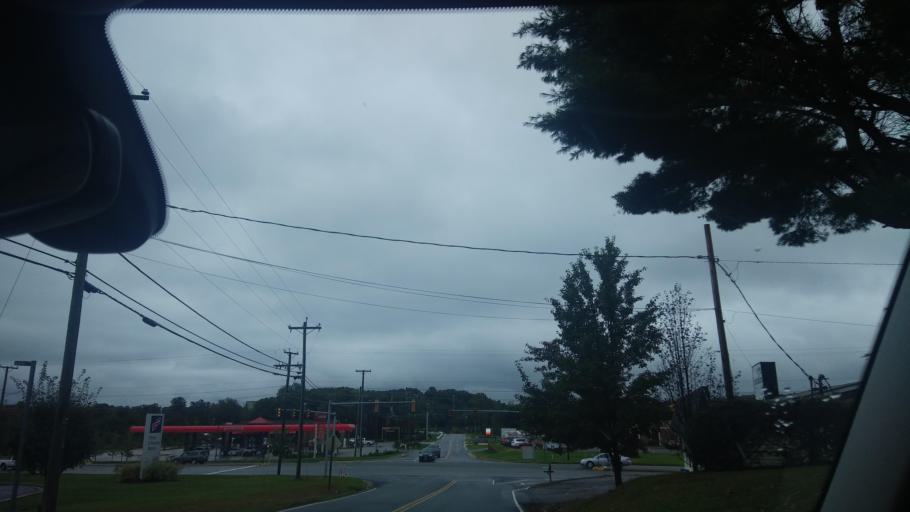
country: US
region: Virginia
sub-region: City of Galax
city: Galax
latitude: 36.6870
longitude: -80.8853
